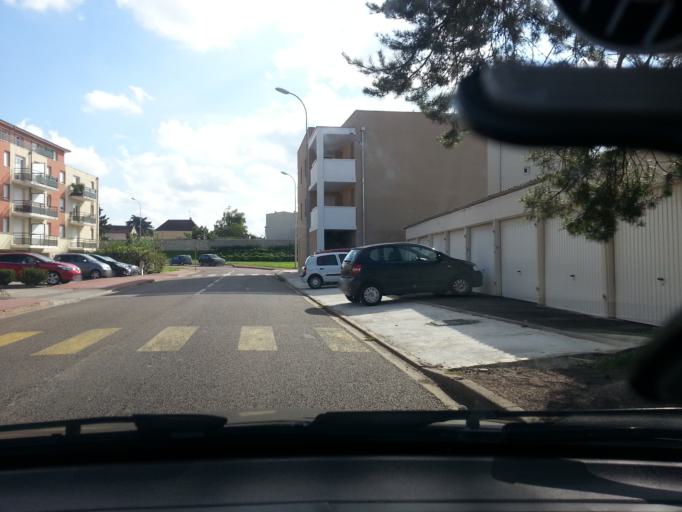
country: FR
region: Bourgogne
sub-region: Departement de Saone-et-Loire
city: Chalon-sur-Saone
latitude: 46.8008
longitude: 4.8589
